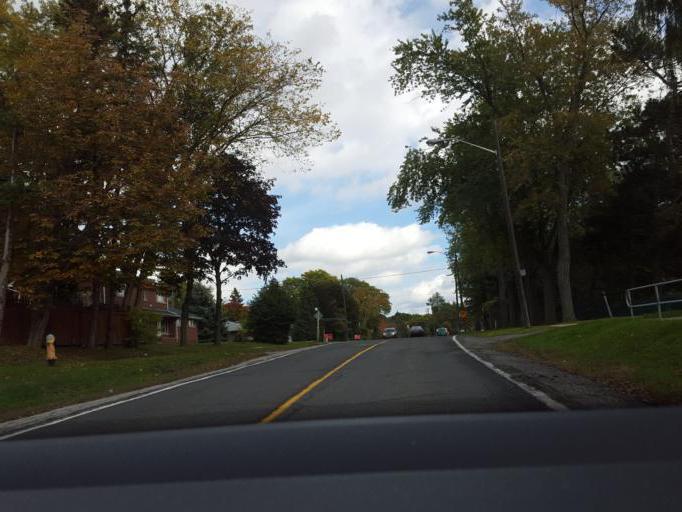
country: CA
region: Ontario
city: Willowdale
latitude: 43.7344
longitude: -79.3608
